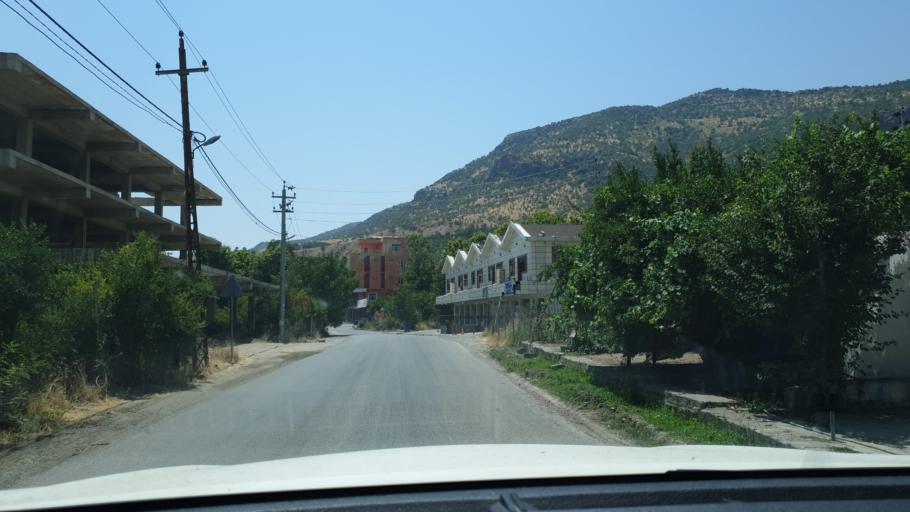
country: IQ
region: Arbil
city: Nahiyat Hiran
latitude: 36.2814
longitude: 44.4945
